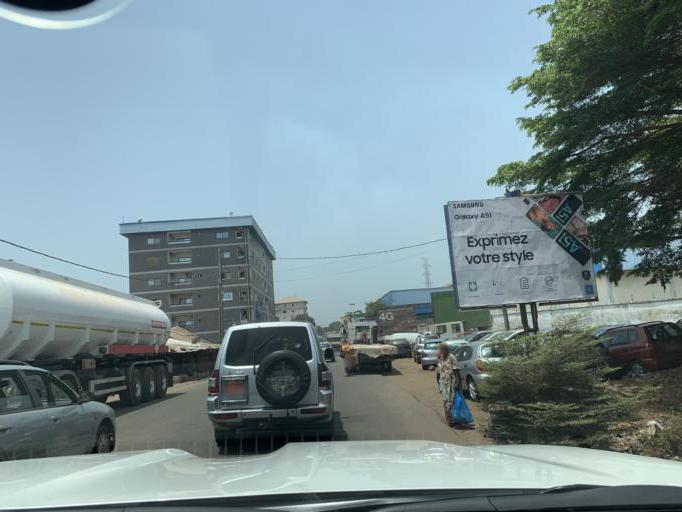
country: GN
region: Conakry
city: Camayenne
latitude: 9.5175
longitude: -13.6996
